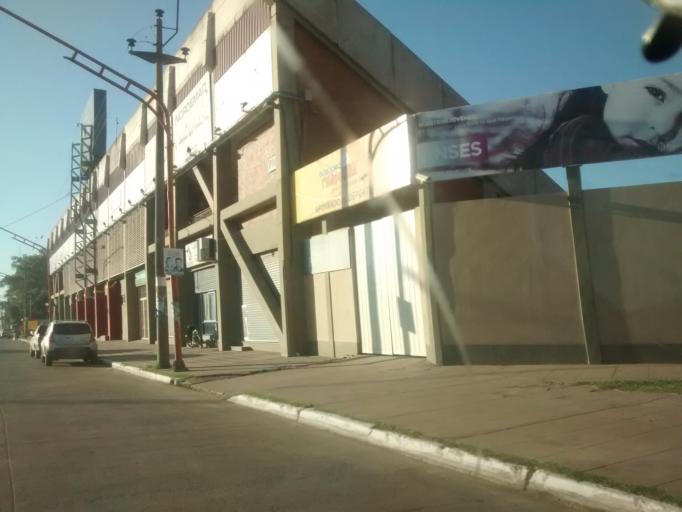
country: AR
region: Chaco
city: Fontana
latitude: -27.4426
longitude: -59.0106
